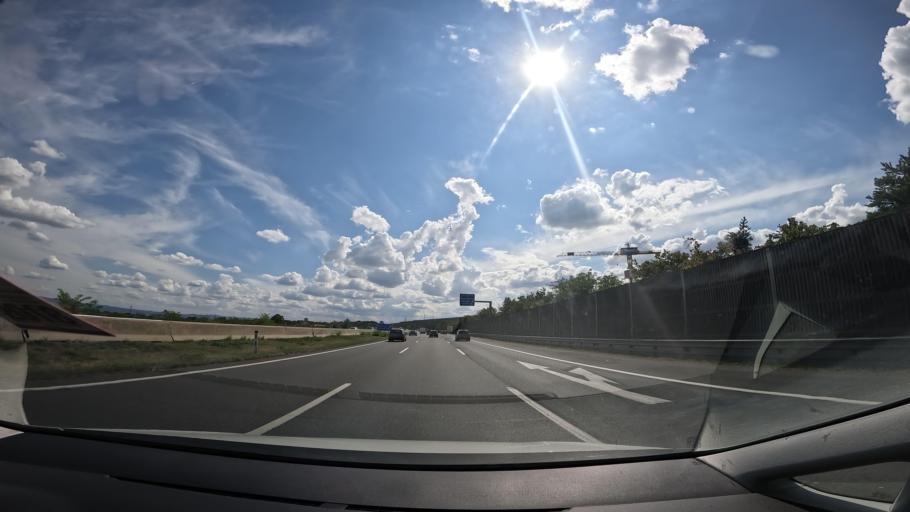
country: AT
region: Lower Austria
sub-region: Politischer Bezirk Wiener Neustadt
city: Theresienfeld
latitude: 47.8629
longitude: 16.1888
